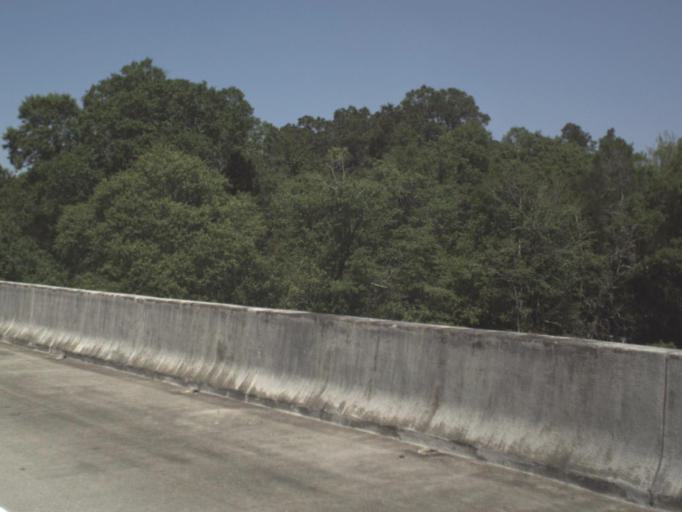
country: US
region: Florida
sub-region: Escambia County
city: Cantonment
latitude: 30.5737
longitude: -87.4119
